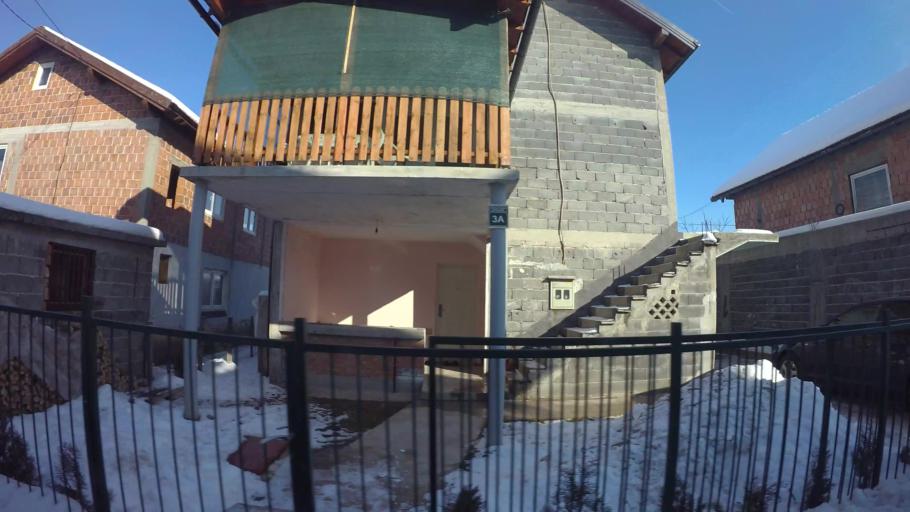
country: BA
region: Federation of Bosnia and Herzegovina
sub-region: Kanton Sarajevo
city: Sarajevo
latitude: 43.8115
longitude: 18.3213
